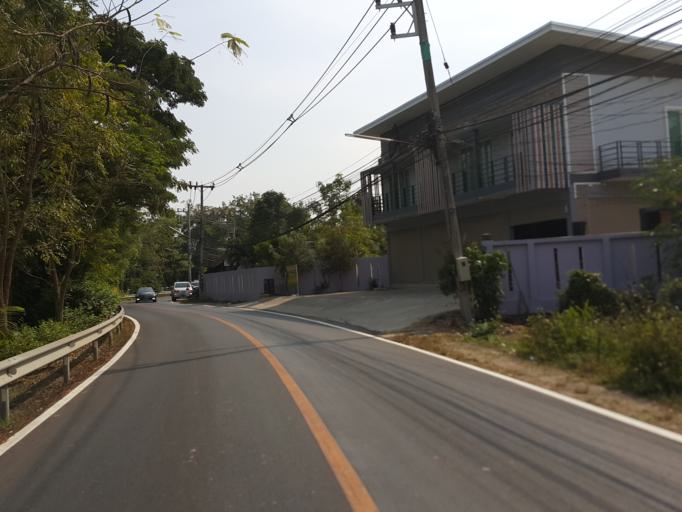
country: TH
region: Chiang Mai
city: Saraphi
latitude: 18.6819
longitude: 98.9839
